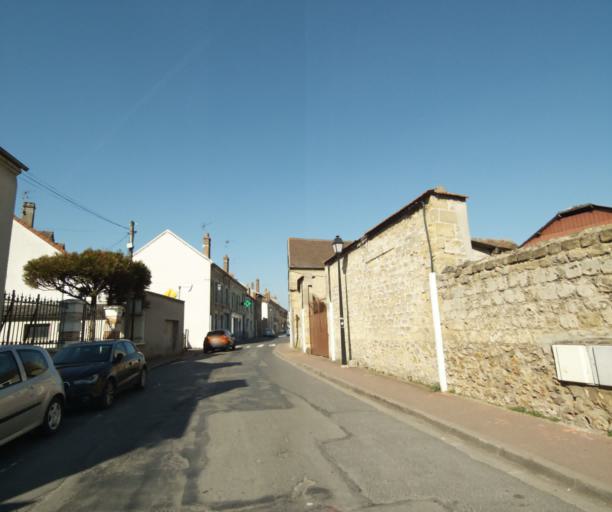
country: FR
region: Ile-de-France
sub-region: Departement du Val-d'Oise
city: Cergy
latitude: 49.0351
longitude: 2.0617
